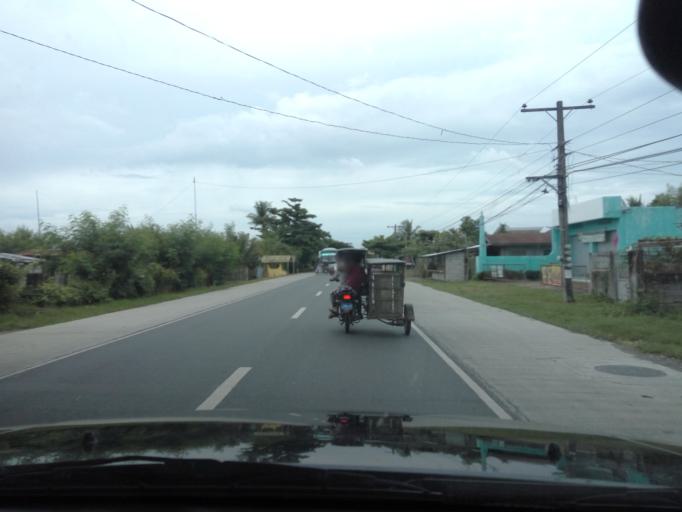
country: PH
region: Central Luzon
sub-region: Province of Nueva Ecija
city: Concepcion
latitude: 15.4479
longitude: 120.8104
